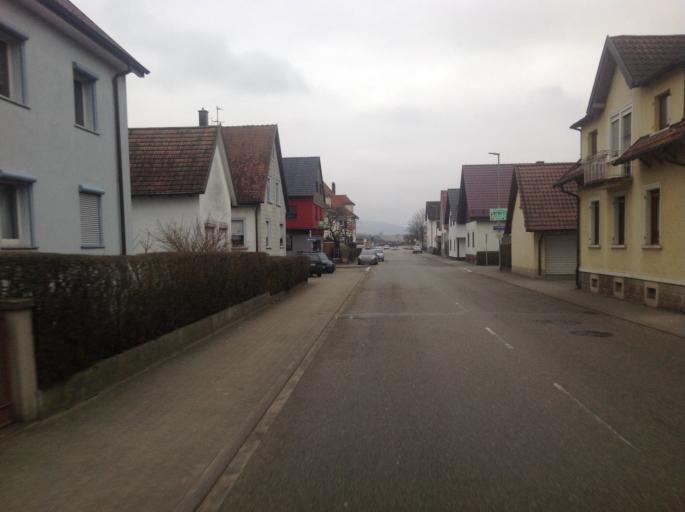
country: DE
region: Baden-Wuerttemberg
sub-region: Karlsruhe Region
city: Iffezheim
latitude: 48.8210
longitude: 8.1474
